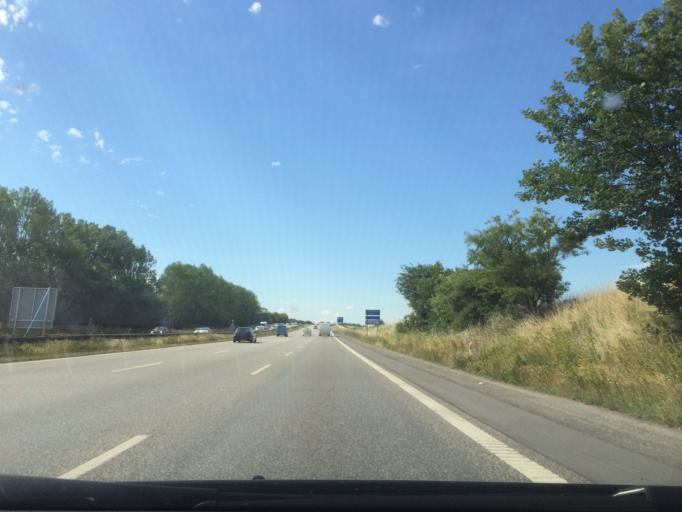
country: DK
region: Zealand
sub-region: Koge Kommune
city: Koge
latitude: 55.4963
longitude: 12.1720
